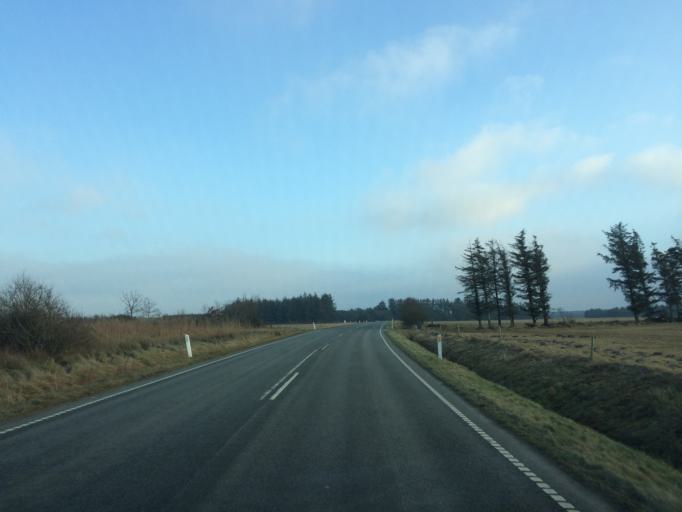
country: DK
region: South Denmark
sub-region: Varde Kommune
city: Oksbol
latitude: 55.7291
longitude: 8.2232
